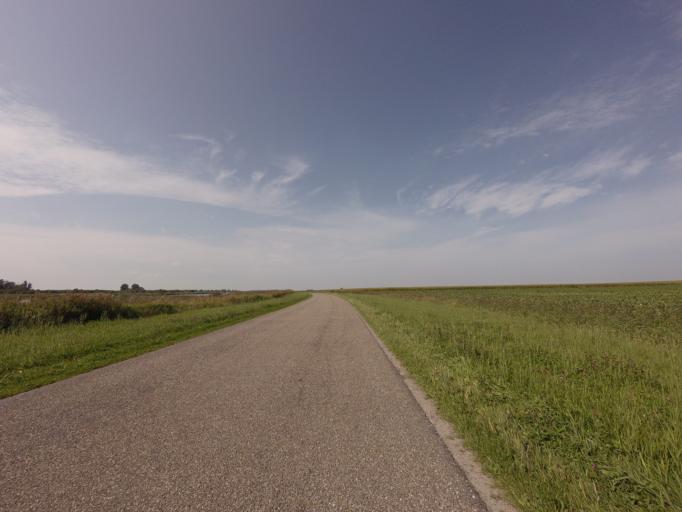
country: NL
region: Groningen
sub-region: Gemeente De Marne
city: Ulrum
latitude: 53.3418
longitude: 6.2886
